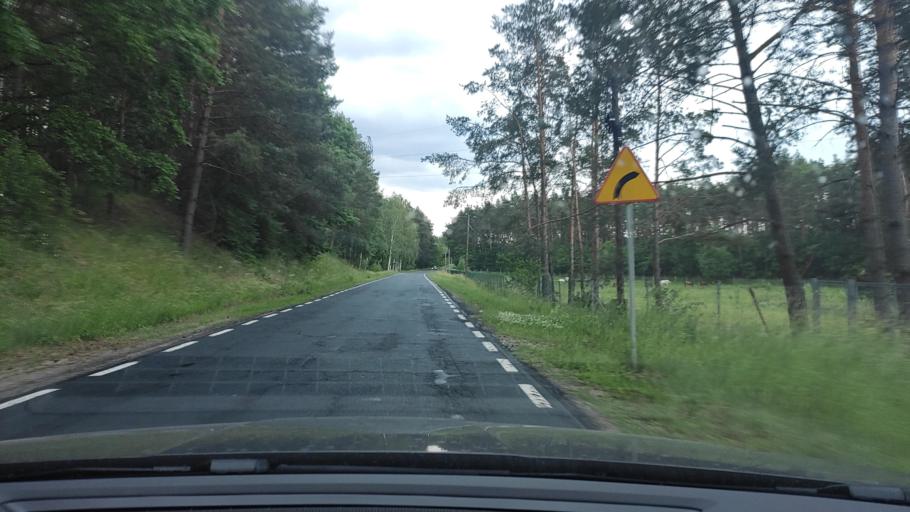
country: PL
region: Greater Poland Voivodeship
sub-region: Powiat poznanski
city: Pobiedziska
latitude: 52.5018
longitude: 17.2273
